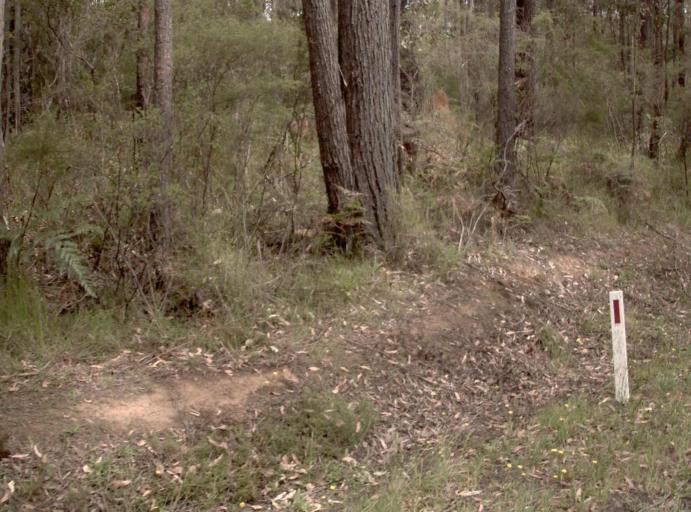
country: AU
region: Victoria
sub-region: Latrobe
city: Traralgon
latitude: -38.0260
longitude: 146.4184
